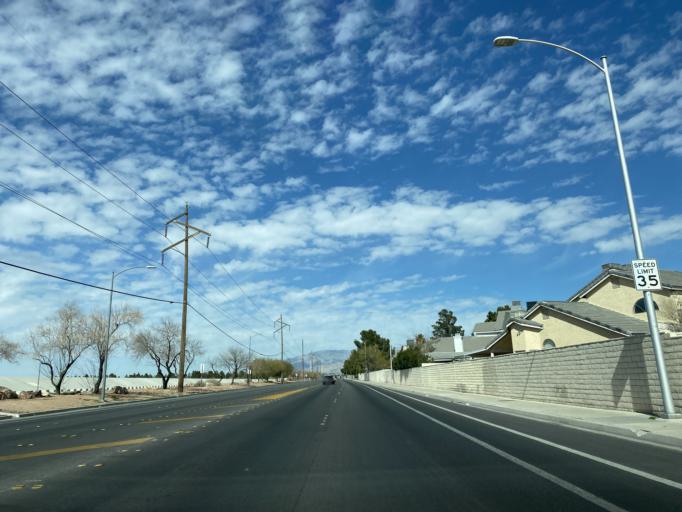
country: US
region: Nevada
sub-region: Clark County
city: Spring Valley
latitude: 36.2261
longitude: -115.2514
